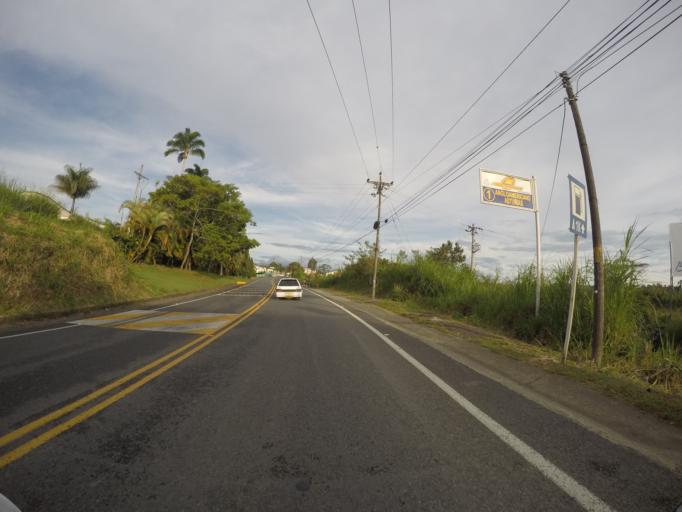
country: CO
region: Risaralda
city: Pereira
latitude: 4.7818
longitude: -75.6986
